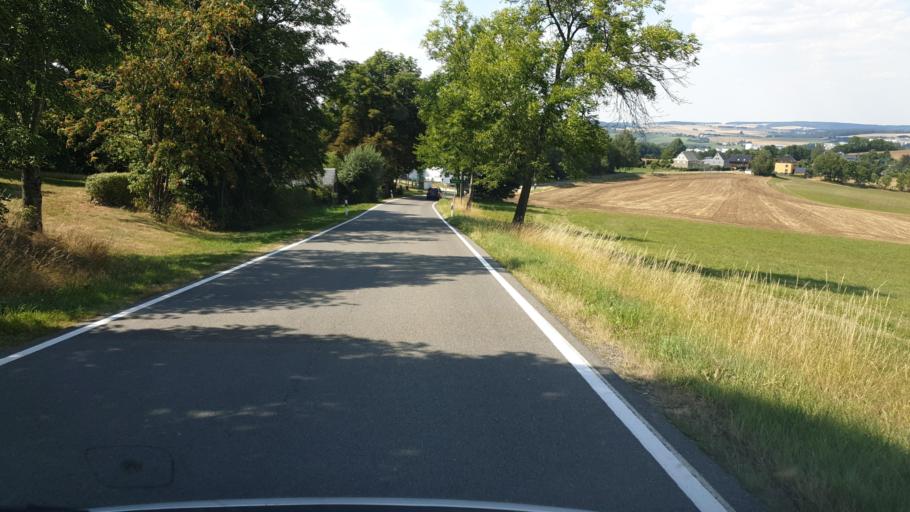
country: DE
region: Saxony
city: Zschopau
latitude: 50.7270
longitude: 13.0871
